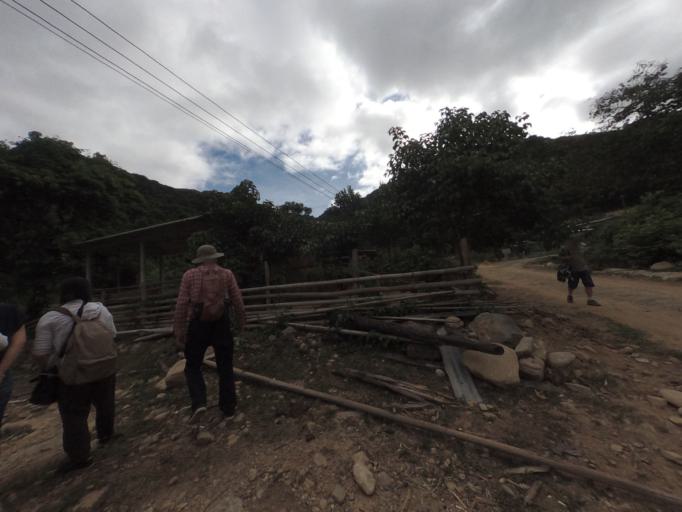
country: VN
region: Thua Thien-Hue
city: A Luoi
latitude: 16.3053
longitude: 107.2145
